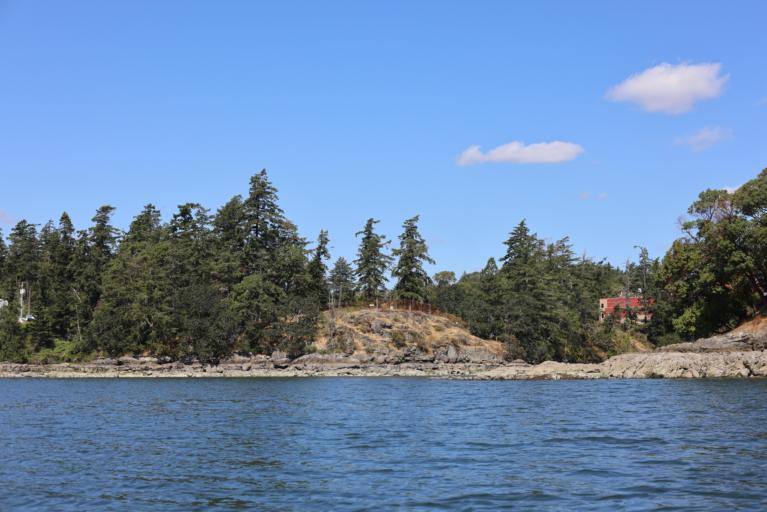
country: CA
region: British Columbia
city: Colwood
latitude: 48.4459
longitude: -123.4475
